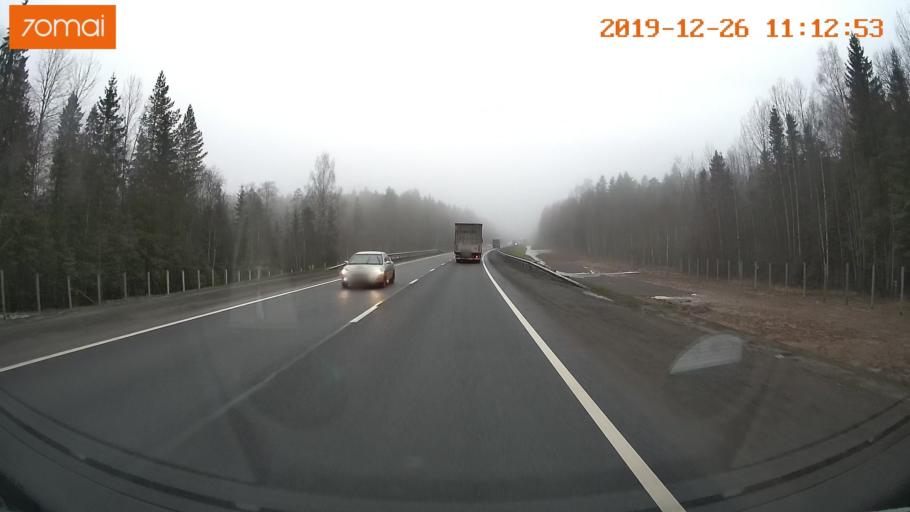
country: RU
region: Vologda
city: Chebsara
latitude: 59.1219
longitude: 39.1649
